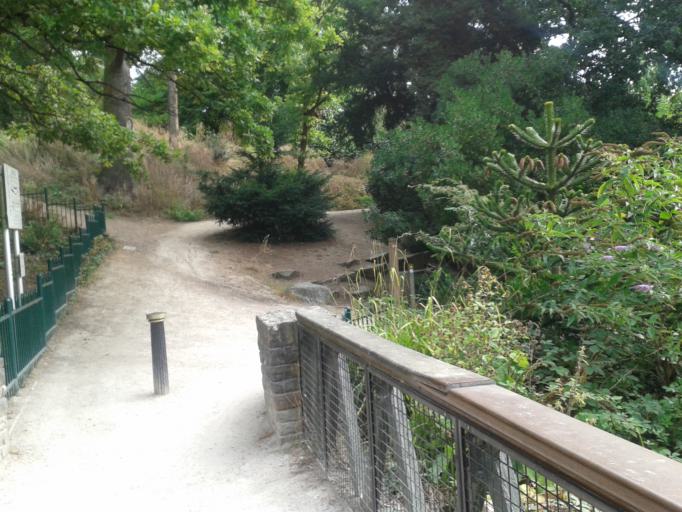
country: GB
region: England
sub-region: Greater London
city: Thornton Heath
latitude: 51.4180
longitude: -0.0676
